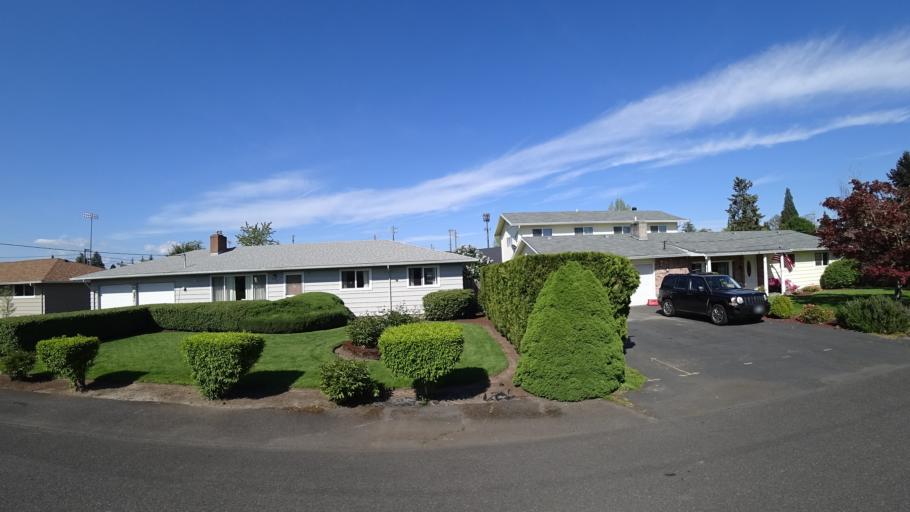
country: US
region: Oregon
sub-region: Washington County
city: Hillsboro
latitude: 45.5270
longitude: -122.9732
